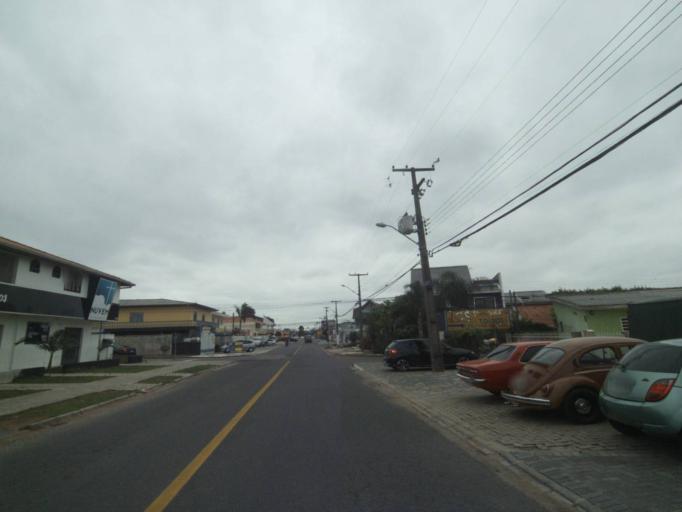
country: BR
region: Parana
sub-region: Sao Jose Dos Pinhais
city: Sao Jose dos Pinhais
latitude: -25.5401
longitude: -49.2573
